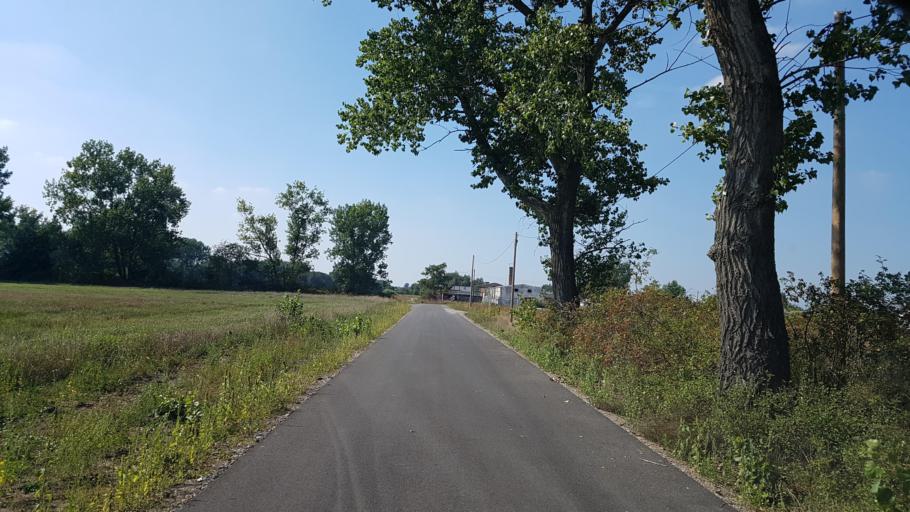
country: DE
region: Brandenburg
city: Nauen
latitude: 52.6813
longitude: 12.9327
